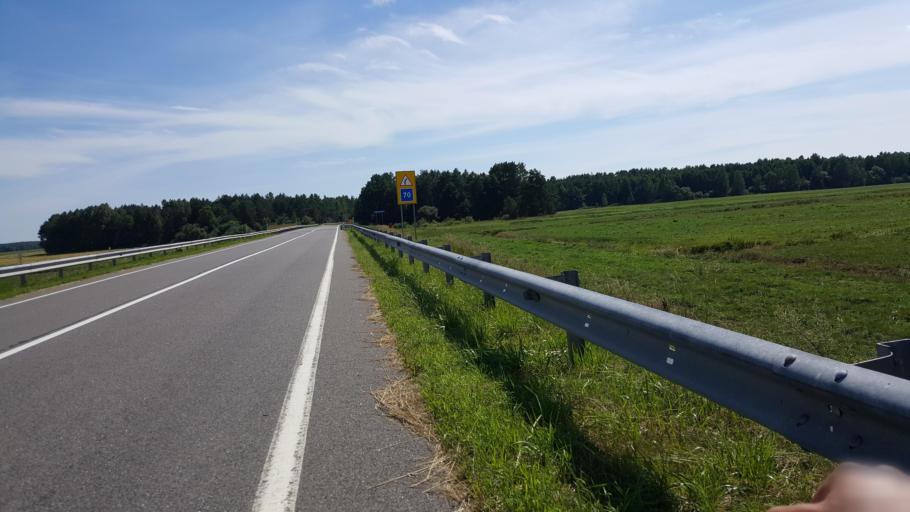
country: BY
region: Brest
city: Zhabinka
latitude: 52.4746
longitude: 24.1554
